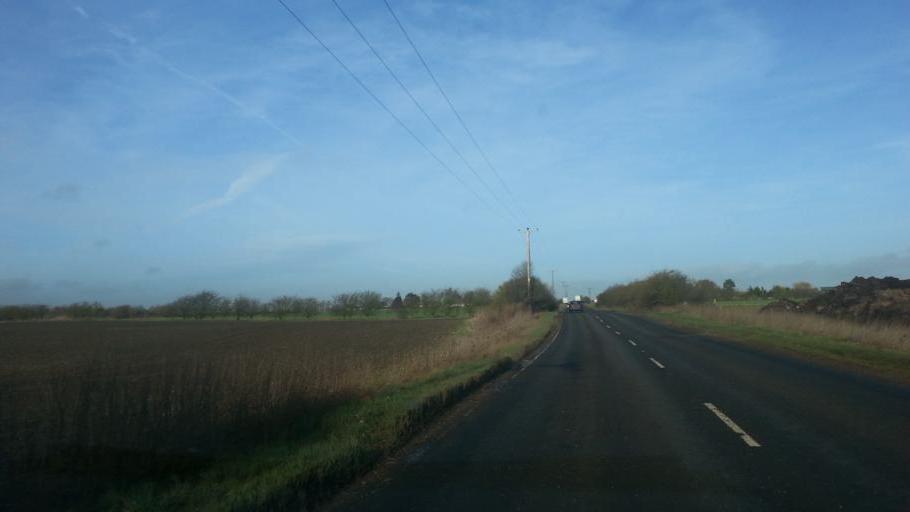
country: GB
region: England
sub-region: Cambridgeshire
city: Warboys
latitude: 52.4124
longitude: -0.1037
